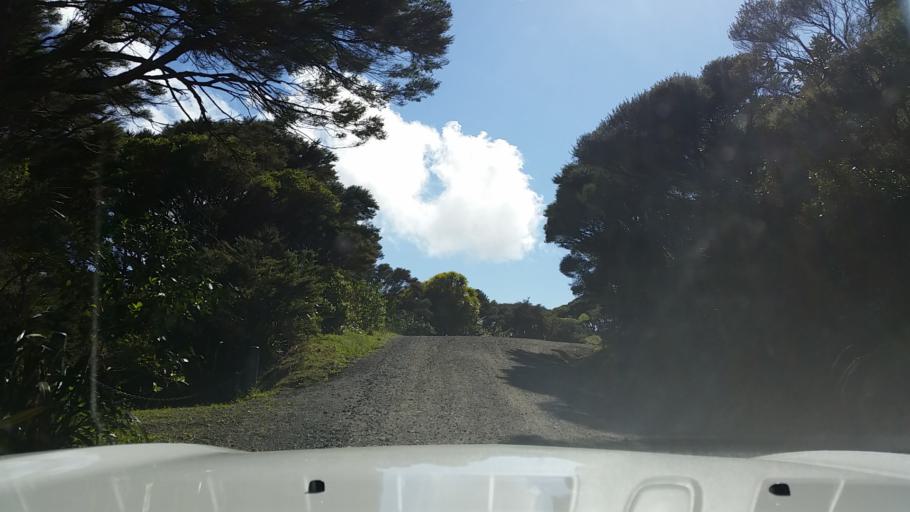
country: NZ
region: Auckland
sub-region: Auckland
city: Titirangi
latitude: -37.0147
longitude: 174.5376
